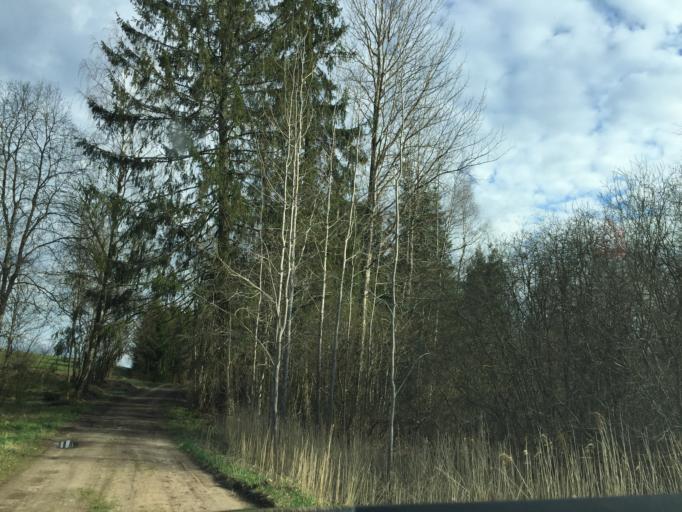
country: LV
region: Aluksnes Rajons
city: Aluksne
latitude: 57.3990
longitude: 26.9848
